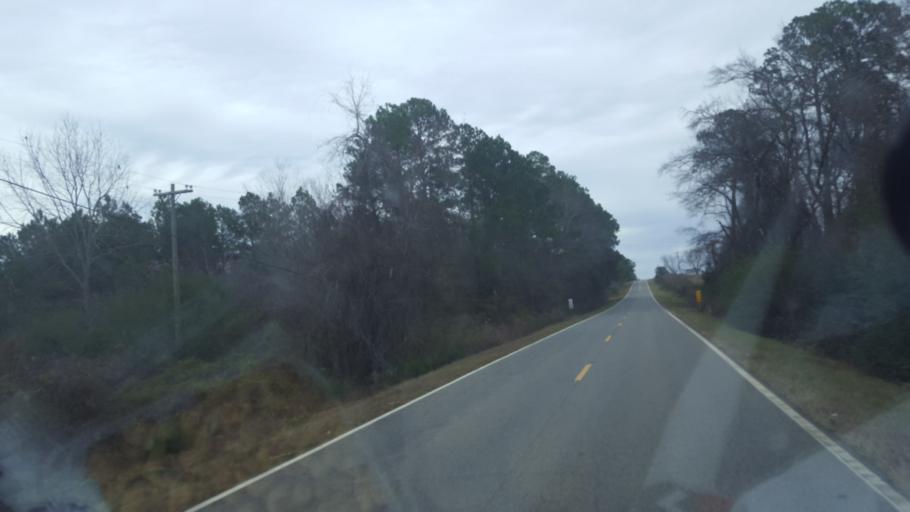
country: US
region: Georgia
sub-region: Ben Hill County
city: Fitzgerald
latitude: 31.7829
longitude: -83.4045
